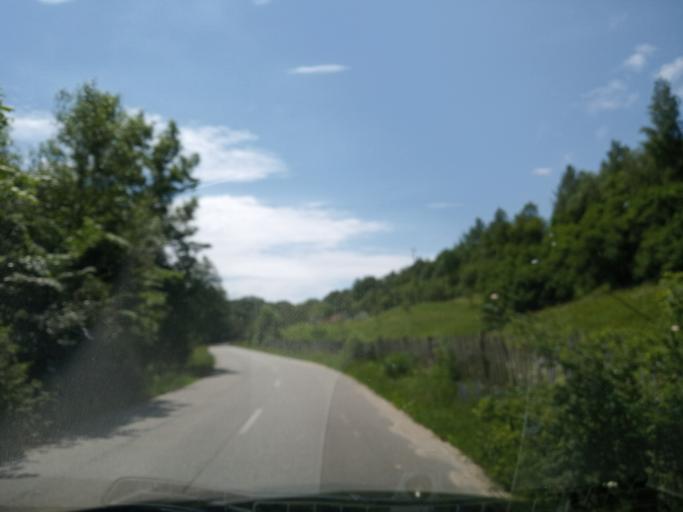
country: RO
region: Hunedoara
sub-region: Oras Petrila
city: Petrila
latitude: 45.4107
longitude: 23.4117
